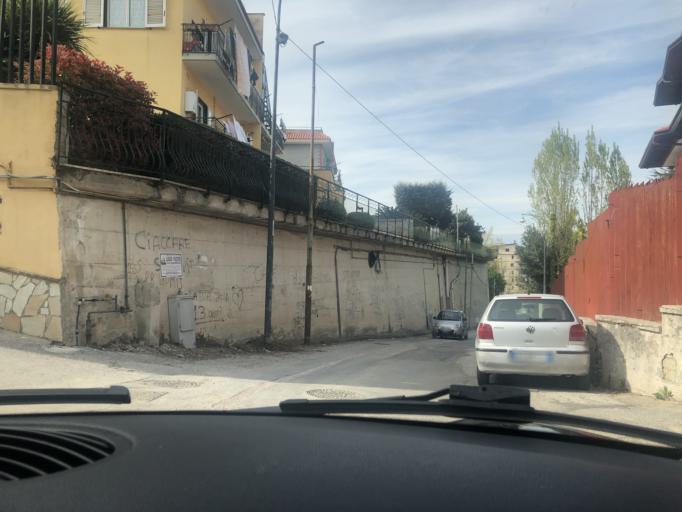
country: IT
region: Campania
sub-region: Provincia di Napoli
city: Torre Caracciolo
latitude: 40.8694
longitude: 14.1933
